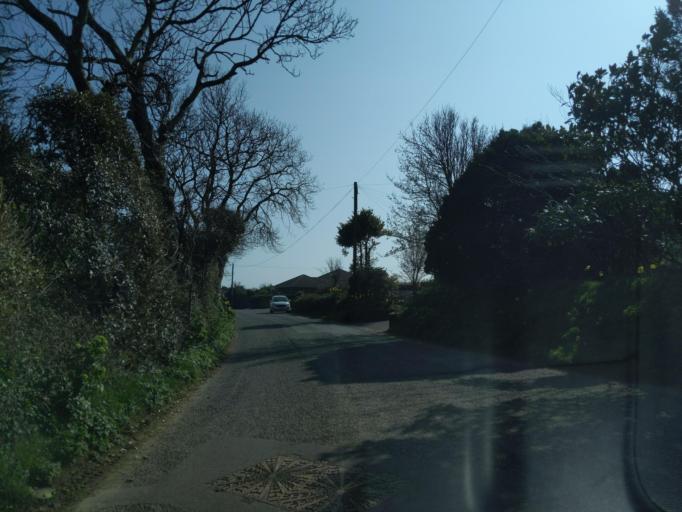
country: GB
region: England
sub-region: Devon
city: Dartmouth
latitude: 50.3136
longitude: -3.6324
